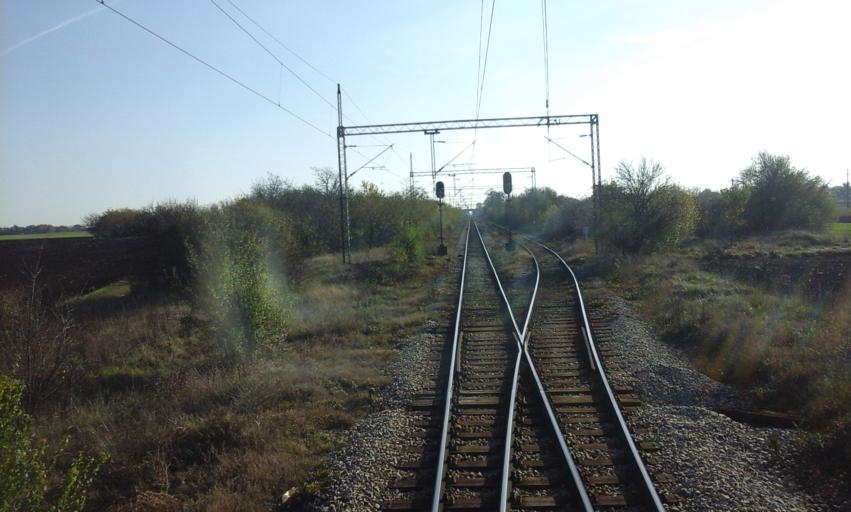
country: RS
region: Autonomna Pokrajina Vojvodina
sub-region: Severnobacki Okrug
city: Mali Igos
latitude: 45.7504
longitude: 19.6488
